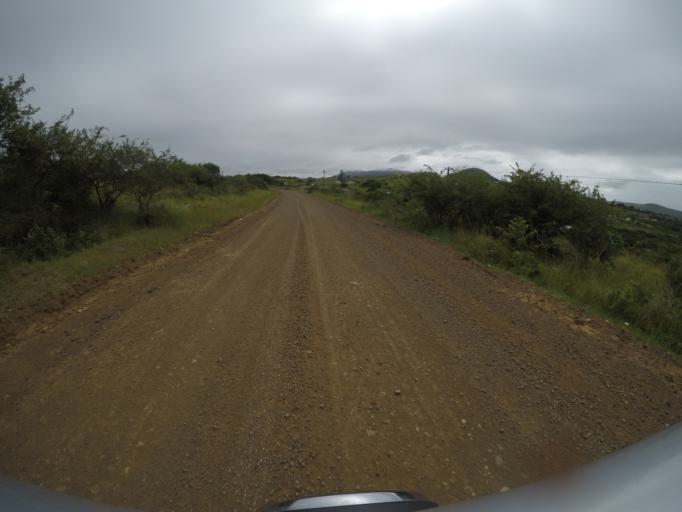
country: ZA
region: KwaZulu-Natal
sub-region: uThungulu District Municipality
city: Empangeni
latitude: -28.6053
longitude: 31.8373
